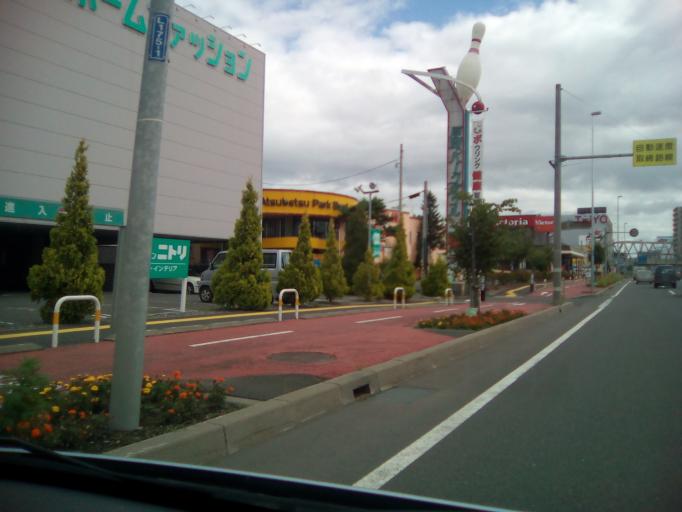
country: JP
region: Hokkaido
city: Ebetsu
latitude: 43.0380
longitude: 141.4662
